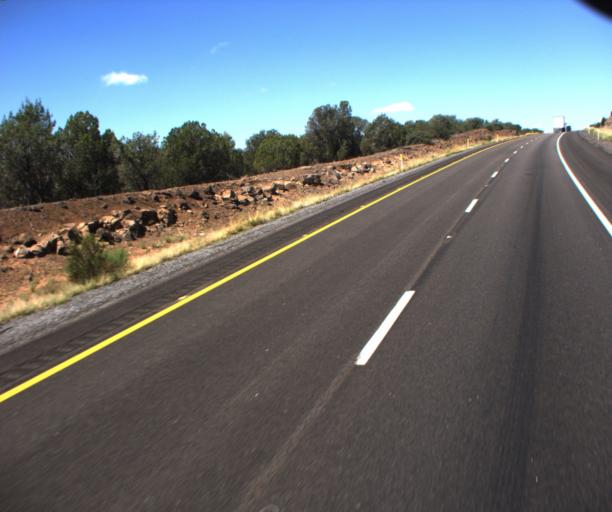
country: US
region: Arizona
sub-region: Mohave County
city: Peach Springs
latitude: 35.1899
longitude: -113.3228
